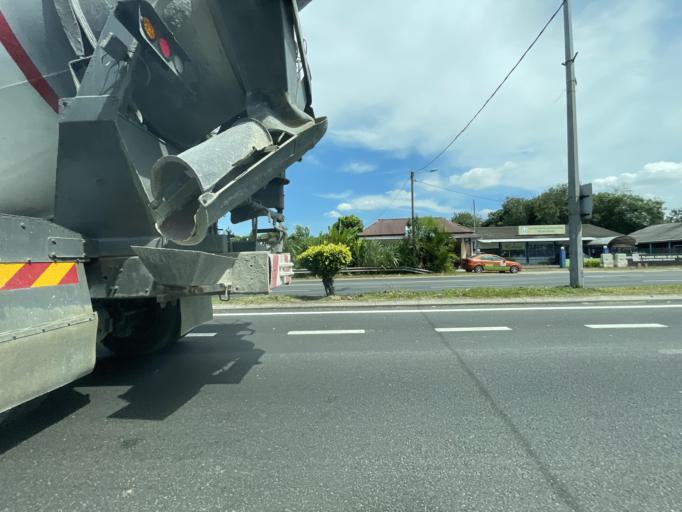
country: MY
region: Melaka
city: Batu Berendam
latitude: 2.2439
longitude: 102.2233
